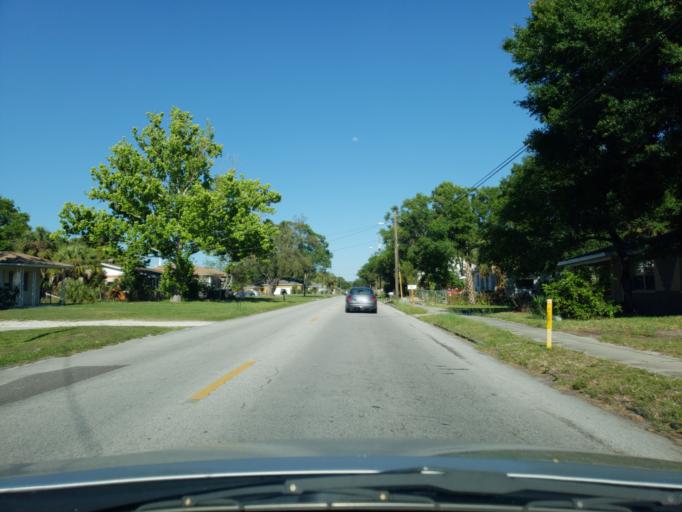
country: US
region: Florida
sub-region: Hillsborough County
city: Tampa
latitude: 27.9520
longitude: -82.4886
